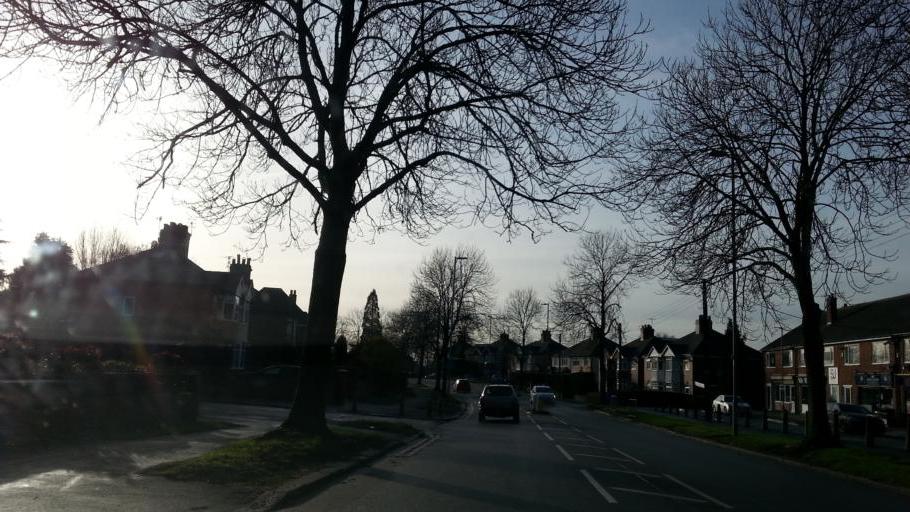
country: GB
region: England
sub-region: Stoke-on-Trent
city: Stoke-on-Trent
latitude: 53.0554
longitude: -2.1387
